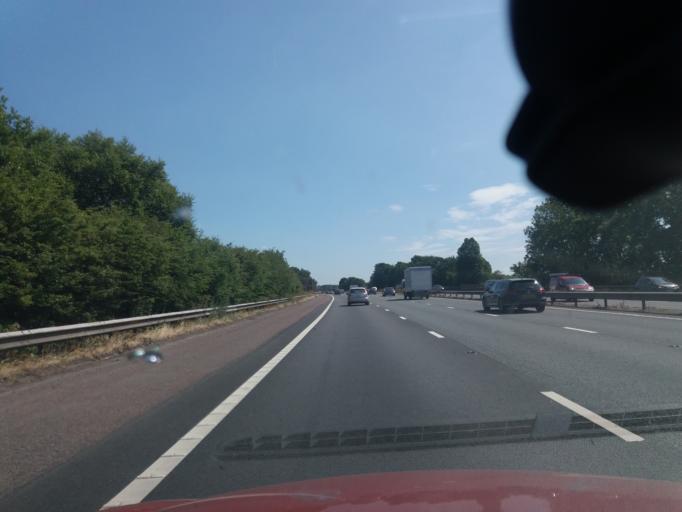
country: GB
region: England
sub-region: Borough of Bolton
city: Horwich
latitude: 53.5847
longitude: -2.5566
